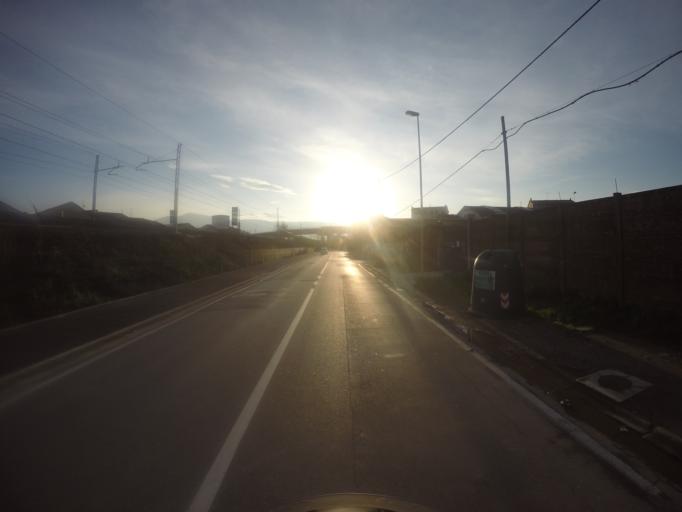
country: IT
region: Tuscany
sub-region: Provincia di Prato
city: Prato
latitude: 43.8920
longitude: 11.0700
